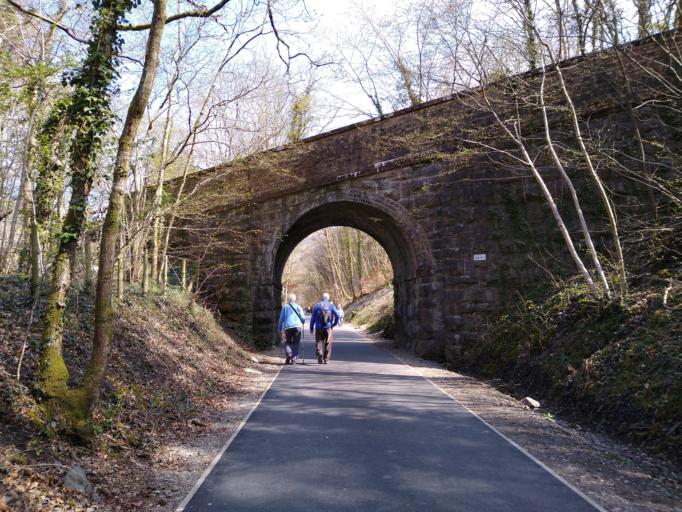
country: GB
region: England
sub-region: Cumbria
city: Keswick
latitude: 54.6067
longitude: -3.1075
